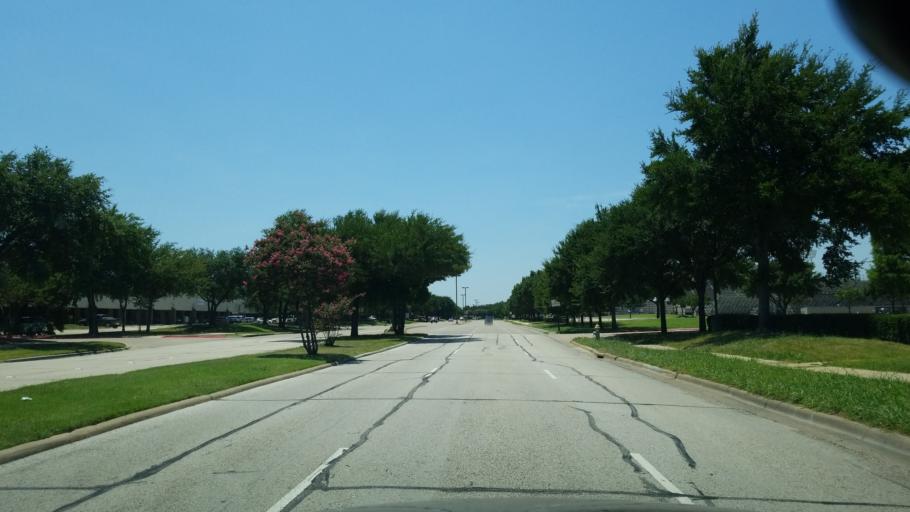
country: US
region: Texas
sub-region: Dallas County
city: Farmers Branch
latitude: 32.9391
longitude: -96.9104
